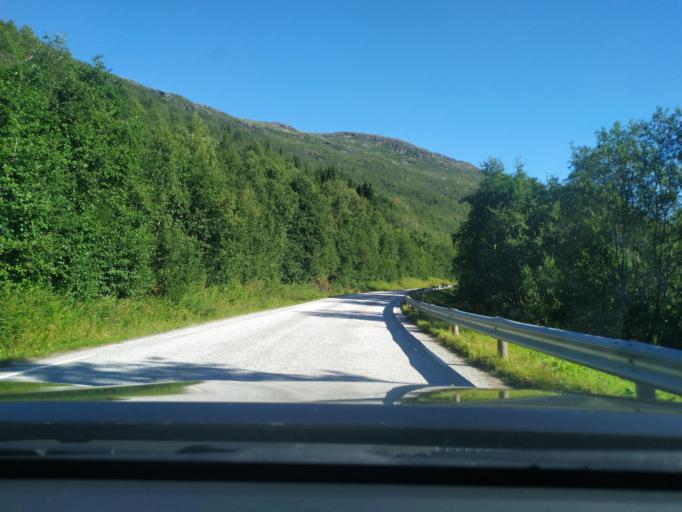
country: NO
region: Troms
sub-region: Dyroy
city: Brostadbotn
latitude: 68.9264
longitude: 17.6403
